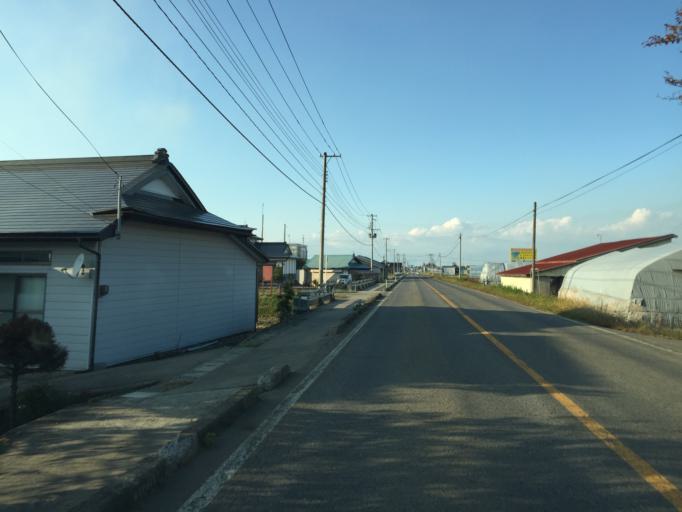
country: JP
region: Fukushima
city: Kitakata
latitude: 37.5473
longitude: 139.9113
